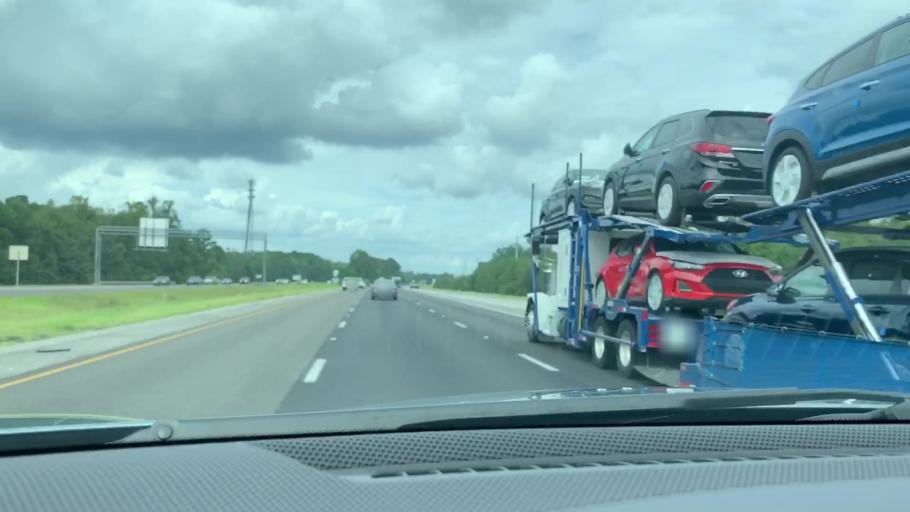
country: US
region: Georgia
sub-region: Liberty County
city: Midway
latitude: 31.7826
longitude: -81.3777
